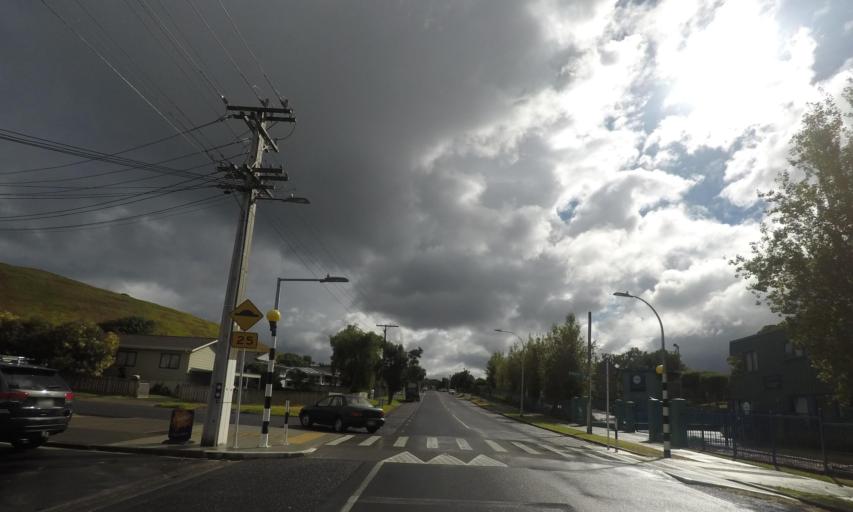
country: NZ
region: Auckland
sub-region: Auckland
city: Mangere
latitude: -36.9546
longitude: 174.7853
